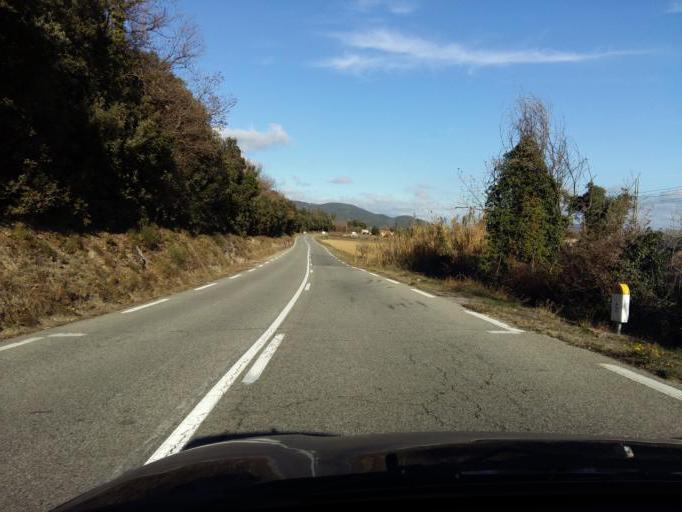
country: FR
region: Rhone-Alpes
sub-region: Departement de l'Ardeche
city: Bourg-Saint-Andeol
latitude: 44.4094
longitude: 4.6504
